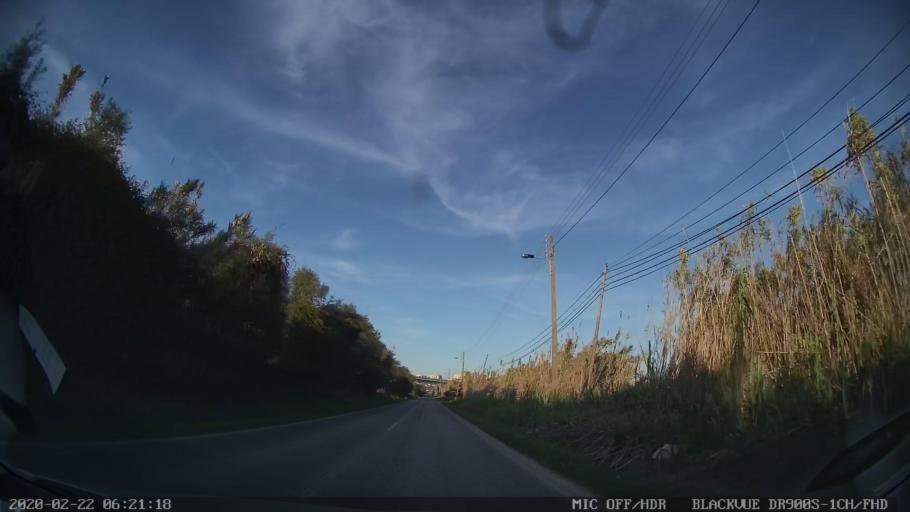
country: PT
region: Lisbon
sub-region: Alenquer
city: Carregado
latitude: 39.0163
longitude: -8.9813
